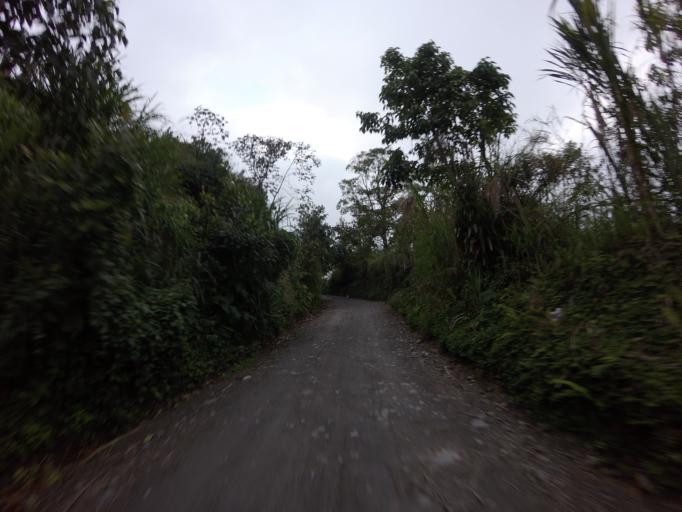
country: CO
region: Caldas
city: Marquetalia
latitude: 5.3565
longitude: -75.0767
